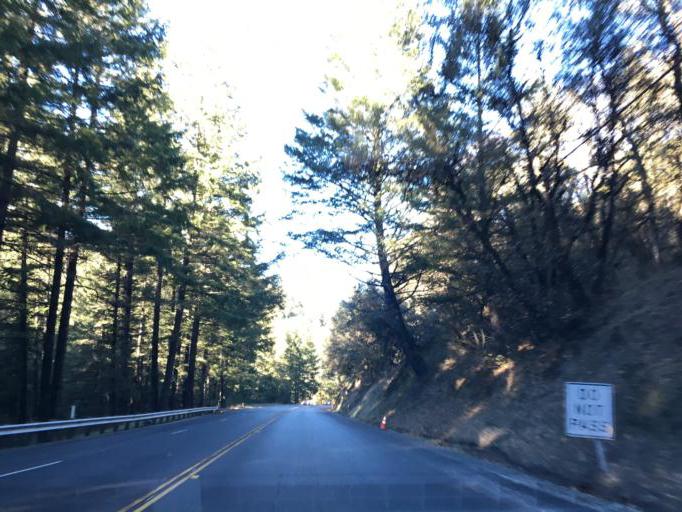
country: US
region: California
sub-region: Mendocino County
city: Laytonville
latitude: 39.7923
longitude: -123.5425
